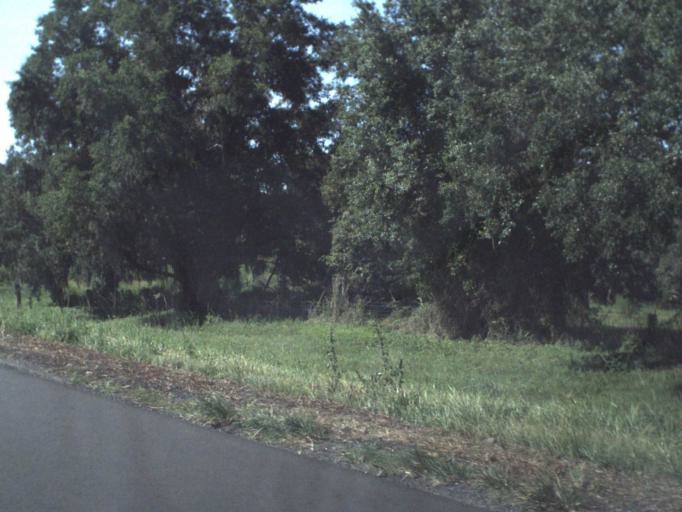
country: US
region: Florida
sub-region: Alachua County
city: Alachua
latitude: 29.7818
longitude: -82.5125
